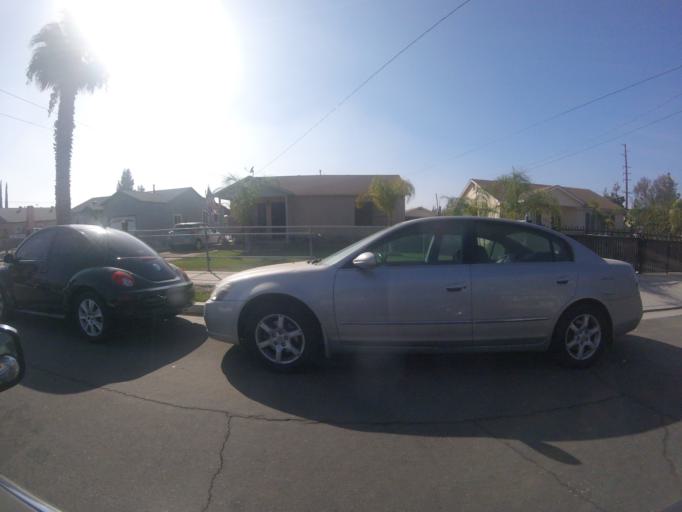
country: US
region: California
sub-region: San Bernardino County
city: Redlands
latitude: 34.0731
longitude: -117.1835
